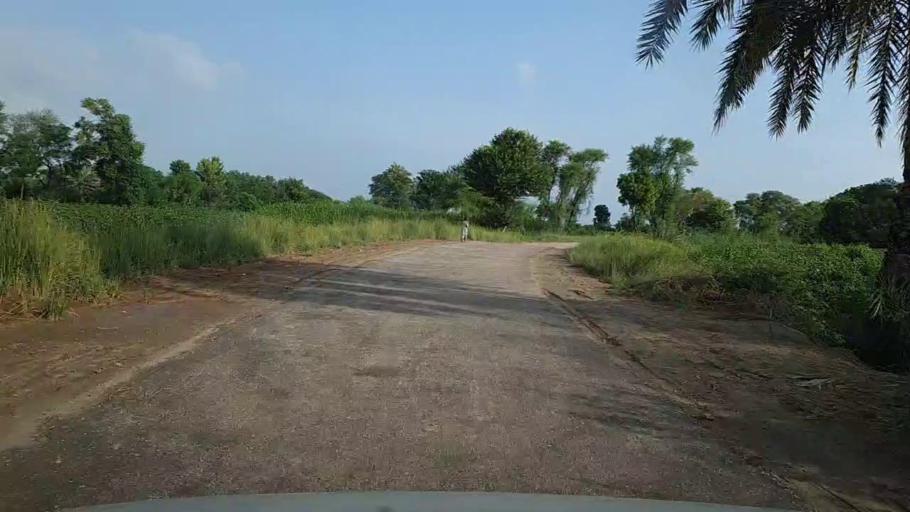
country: PK
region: Sindh
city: Pad Idan
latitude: 26.8012
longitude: 68.2361
